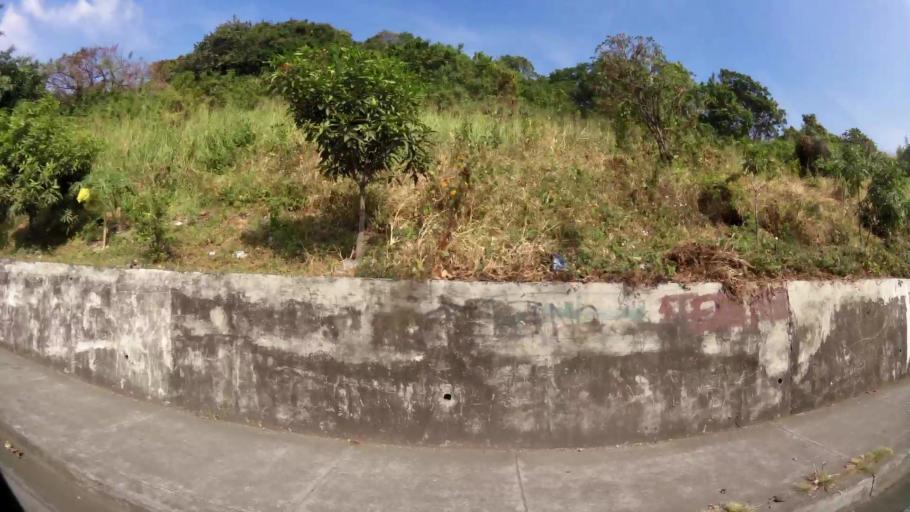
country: EC
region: Guayas
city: Guayaquil
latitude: -2.1848
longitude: -79.9047
